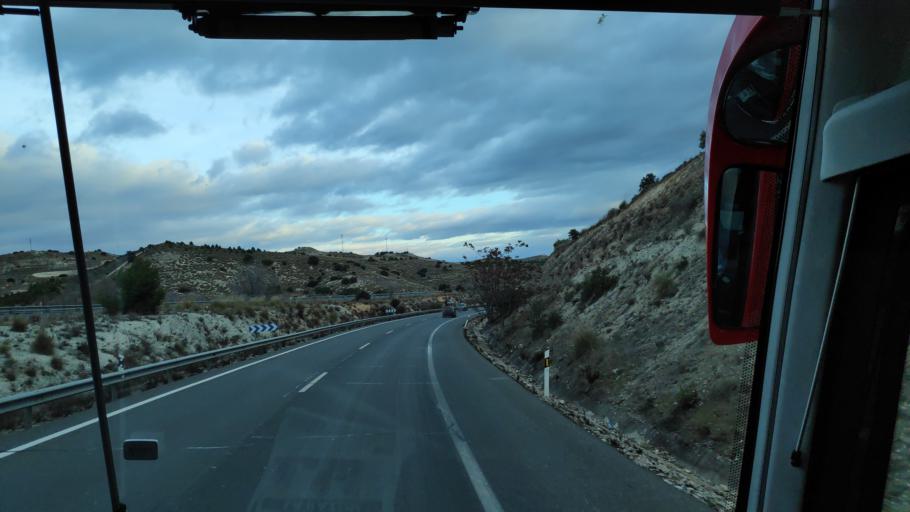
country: ES
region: Madrid
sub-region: Provincia de Madrid
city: Villarejo de Salvanes
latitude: 40.1484
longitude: -3.2213
